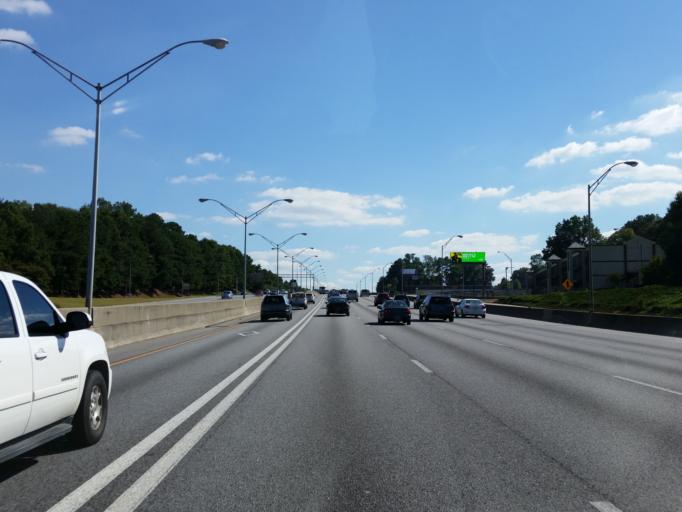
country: US
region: Georgia
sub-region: Fulton County
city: Hapeville
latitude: 33.6807
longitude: -84.3986
